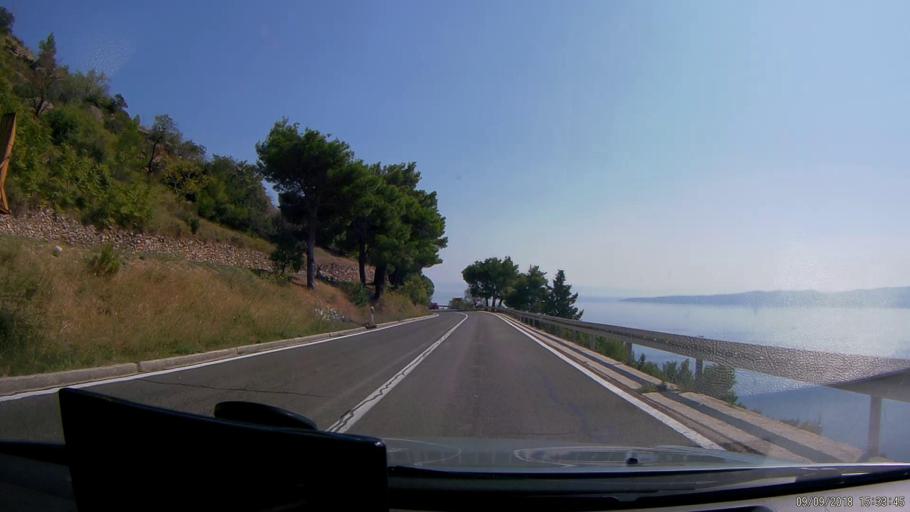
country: HR
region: Splitsko-Dalmatinska
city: Donja Brela
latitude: 43.3917
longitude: 16.8999
